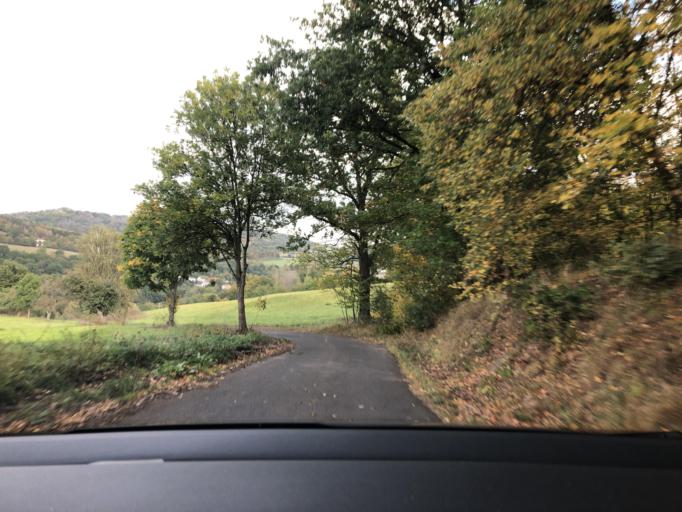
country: CZ
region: Ustecky
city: Velke Brezno
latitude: 50.6262
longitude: 14.1591
